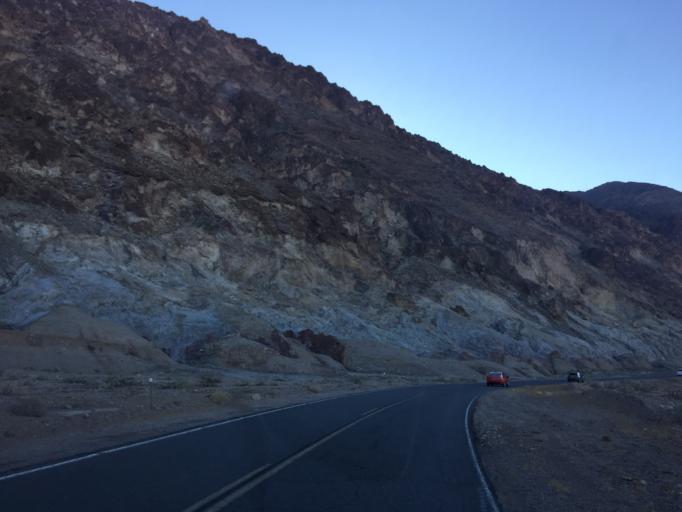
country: US
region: Nevada
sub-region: Nye County
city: Beatty
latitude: 36.1775
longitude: -116.7643
